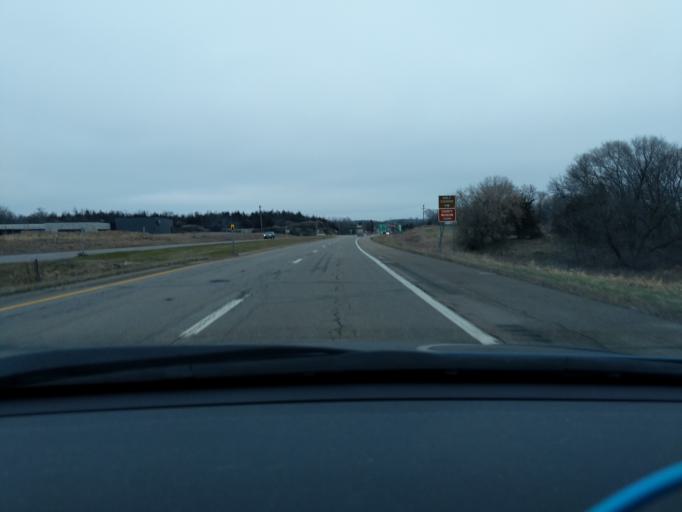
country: US
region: Minnesota
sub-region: Yellow Medicine County
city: Granite Falls
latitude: 44.7999
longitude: -95.5479
